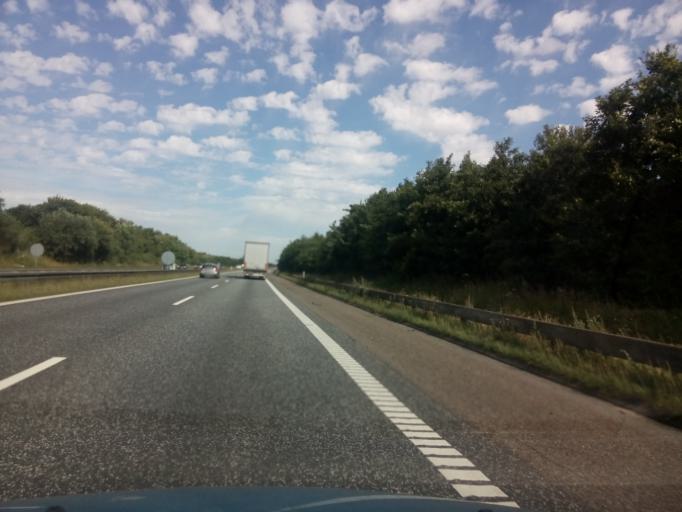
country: DK
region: Central Jutland
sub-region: Favrskov Kommune
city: Hadsten
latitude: 56.3482
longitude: 10.1185
